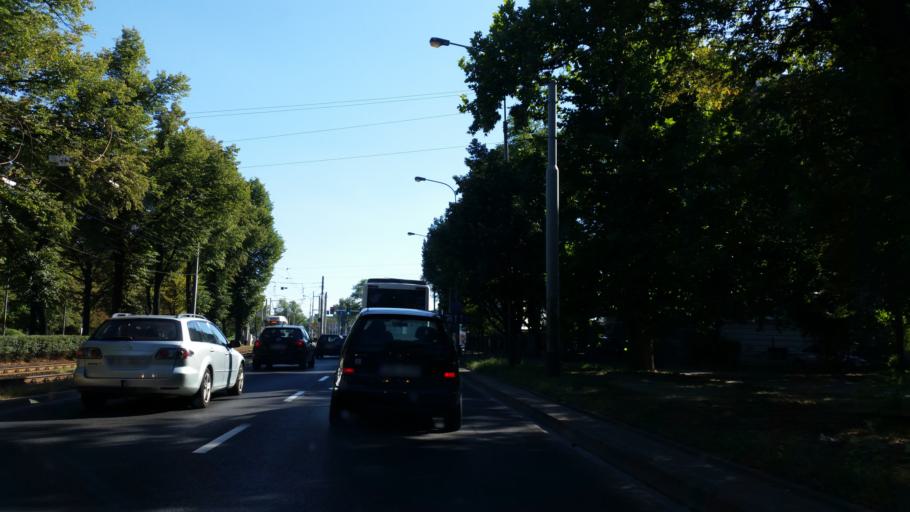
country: PL
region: Lower Silesian Voivodeship
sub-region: Powiat wroclawski
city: Wroclaw
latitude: 51.0811
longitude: 17.0084
